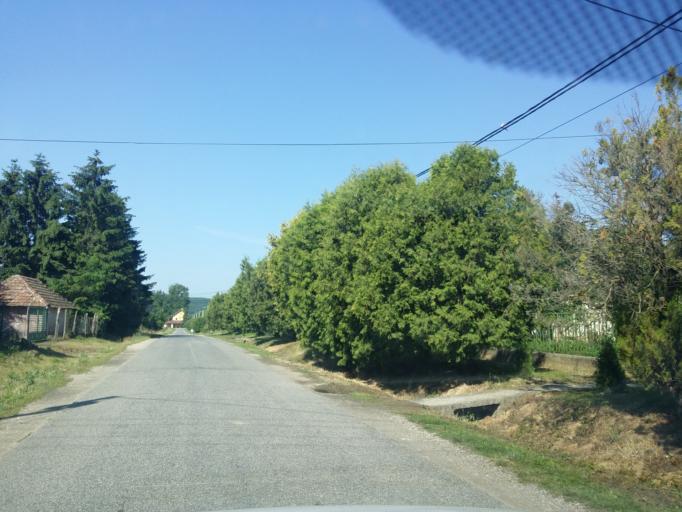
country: HU
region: Zala
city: Zalaszentgrot
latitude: 46.8885
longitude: 17.1089
